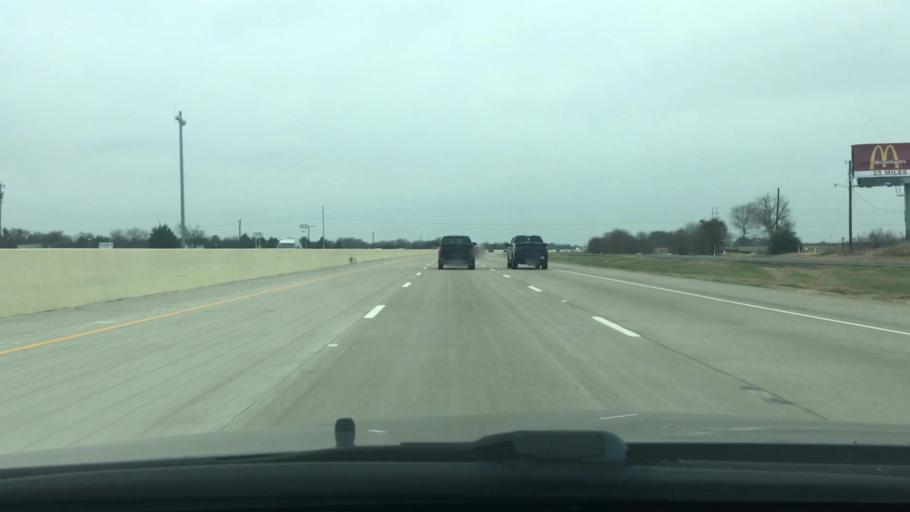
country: US
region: Texas
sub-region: Navarro County
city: Corsicana
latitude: 31.9880
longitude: -96.4254
